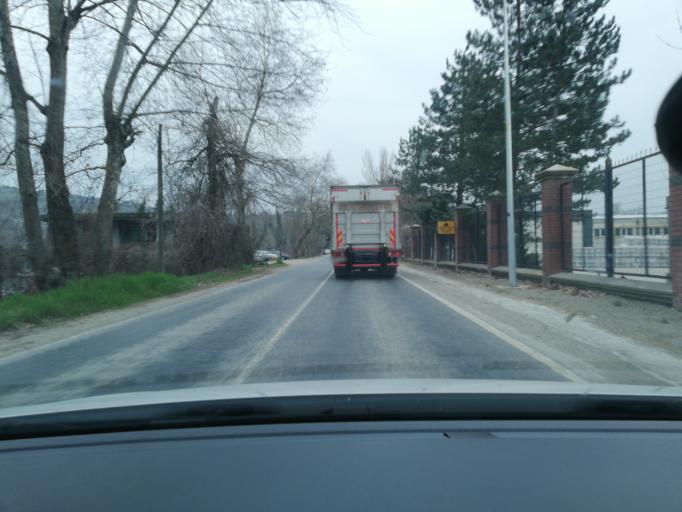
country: TR
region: Zonguldak
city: Gokcebey
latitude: 41.3021
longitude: 32.1229
